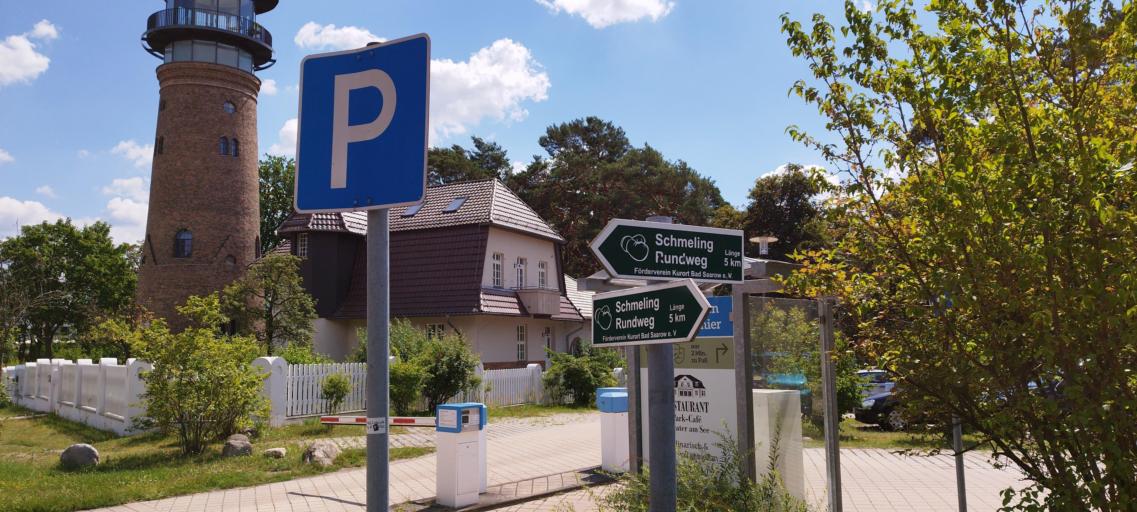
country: DE
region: Brandenburg
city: Bad Saarow
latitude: 52.2926
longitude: 14.0576
